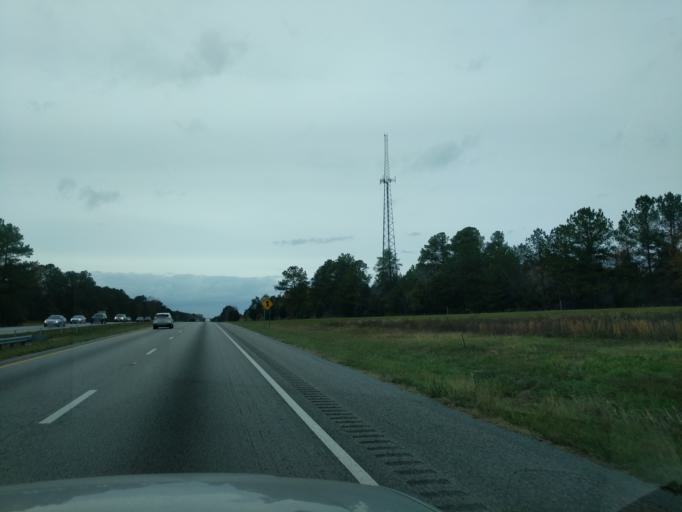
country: US
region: South Carolina
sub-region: Laurens County
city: Joanna
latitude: 34.4399
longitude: -81.7615
